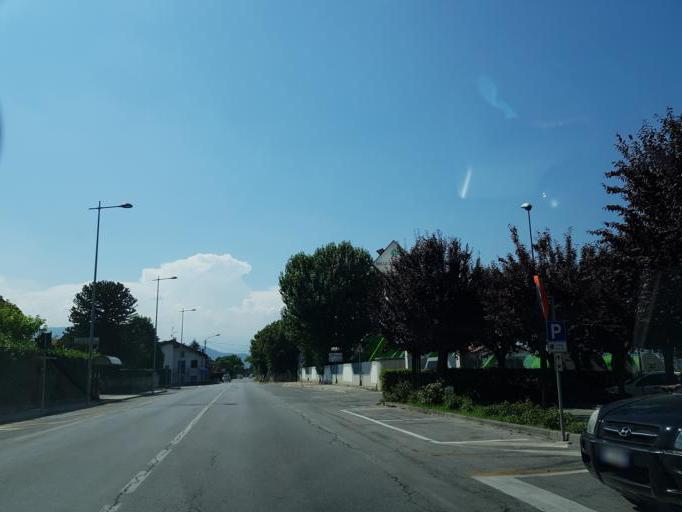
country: IT
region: Piedmont
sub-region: Provincia di Cuneo
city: San Defendente
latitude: 44.3957
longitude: 7.4910
